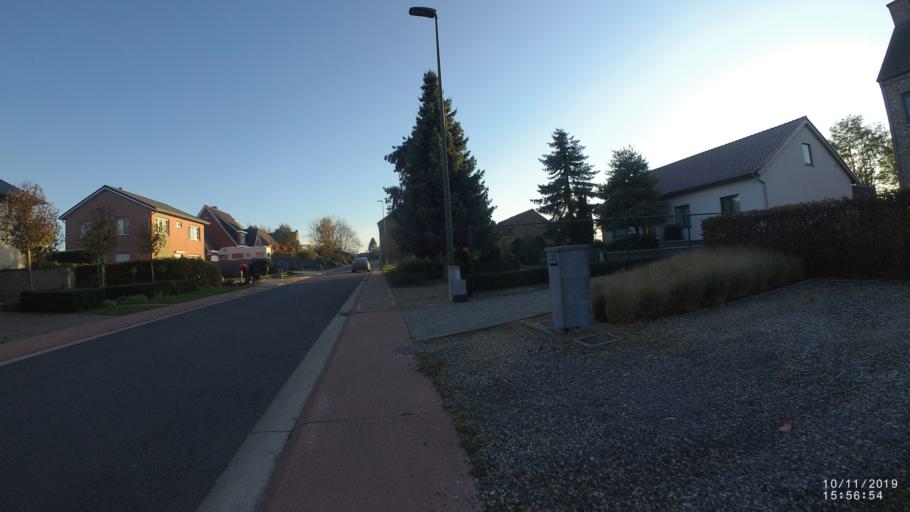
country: BE
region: Flanders
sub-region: Provincie Vlaams-Brabant
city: Lubbeek
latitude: 50.9051
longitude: 4.8856
